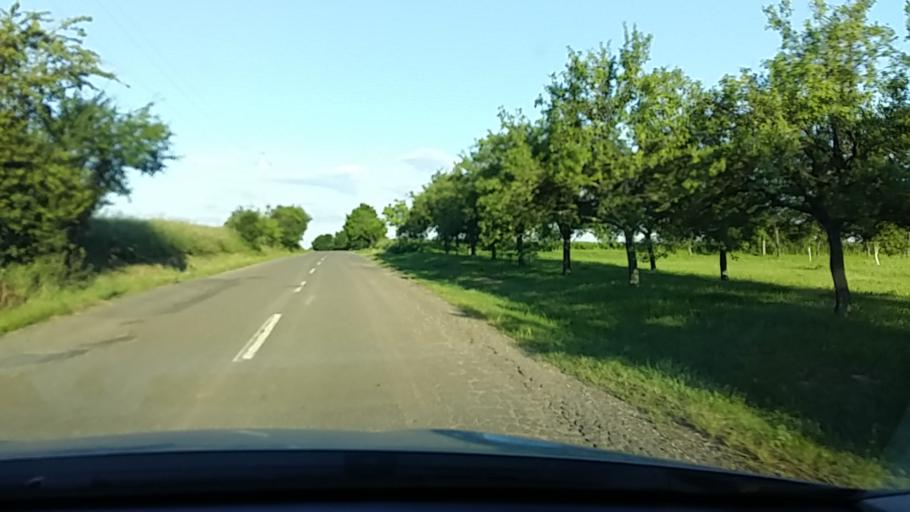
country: HU
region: Nograd
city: Diosjeno
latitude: 47.9069
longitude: 19.0589
